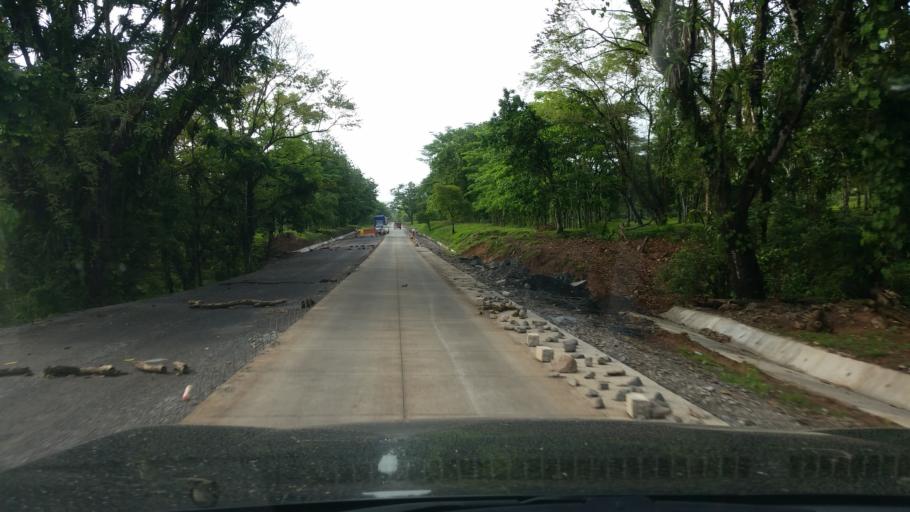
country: NI
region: Matagalpa
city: Rio Blanco
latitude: 13.0874
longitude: -85.0622
